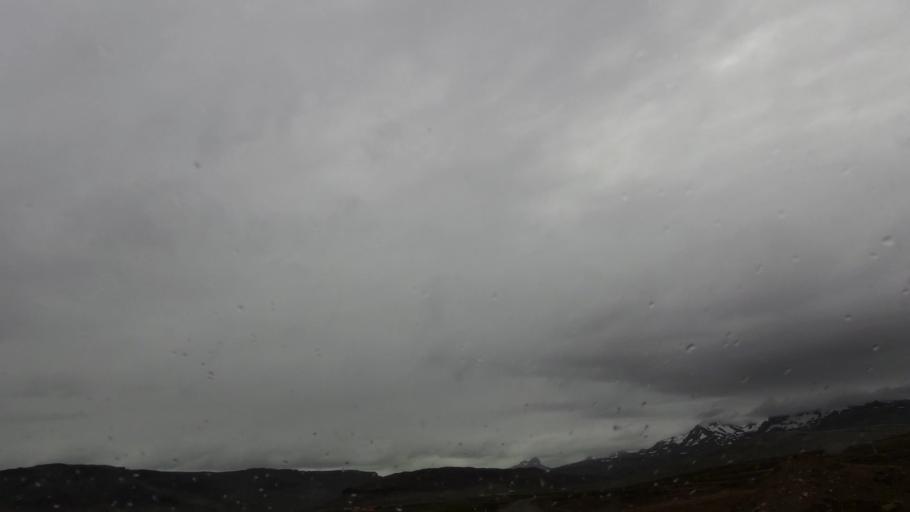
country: IS
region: West
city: Stykkisholmur
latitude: 64.9979
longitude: -22.6867
